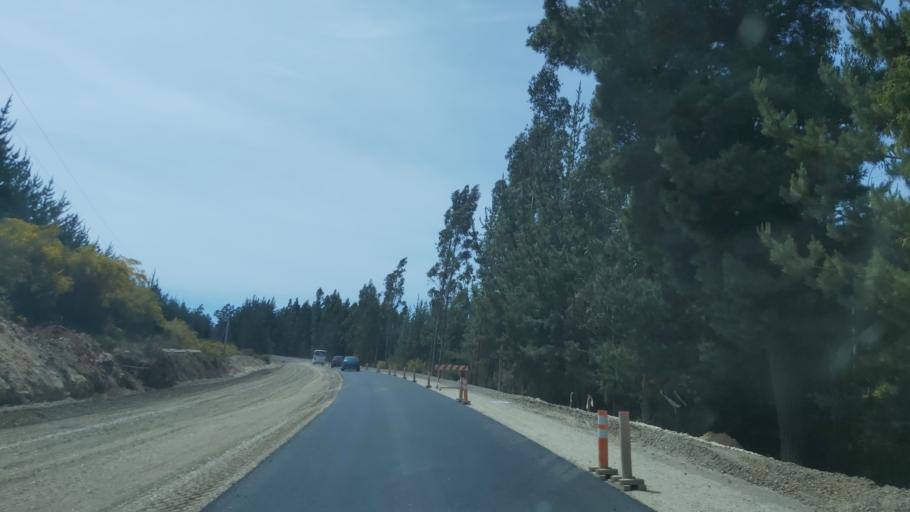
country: CL
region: Maule
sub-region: Provincia de Talca
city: Constitucion
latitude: -35.3818
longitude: -72.4208
